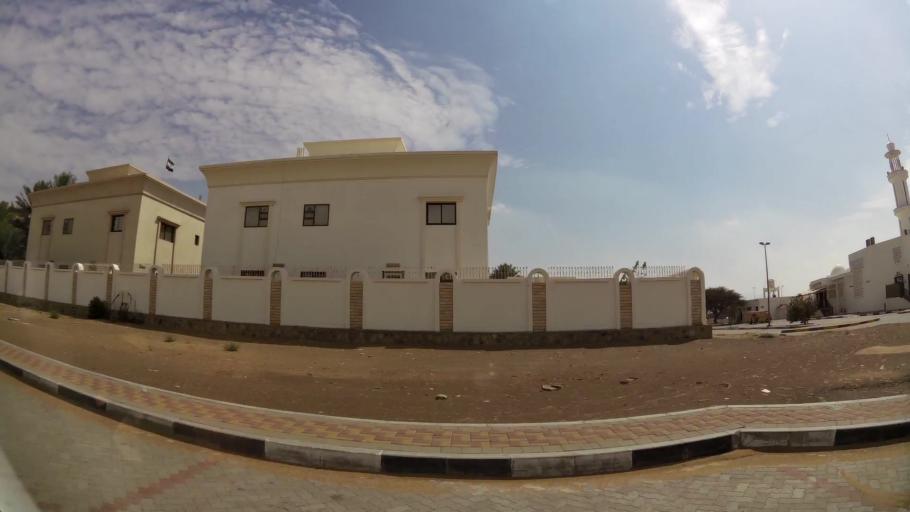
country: AE
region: Abu Dhabi
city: Al Ain
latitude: 24.1902
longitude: 55.7915
